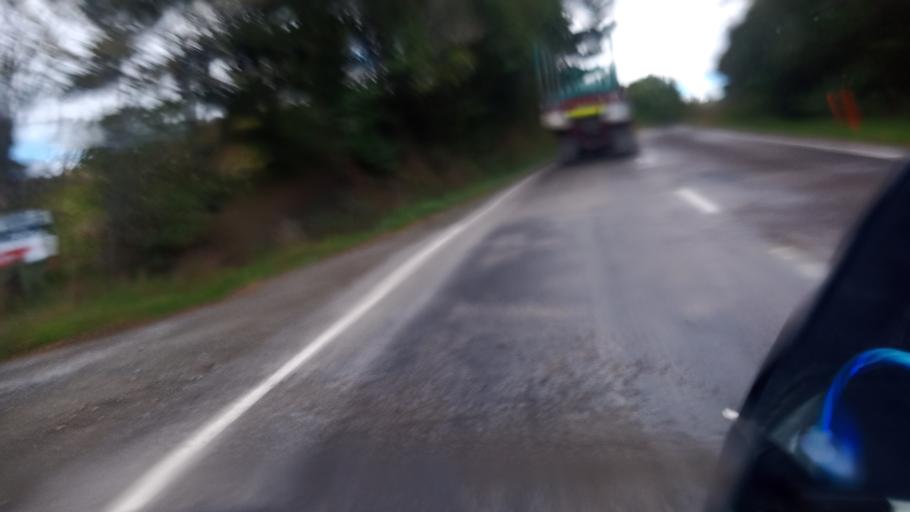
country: NZ
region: Gisborne
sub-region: Gisborne District
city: Gisborne
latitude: -38.0529
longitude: 178.3047
